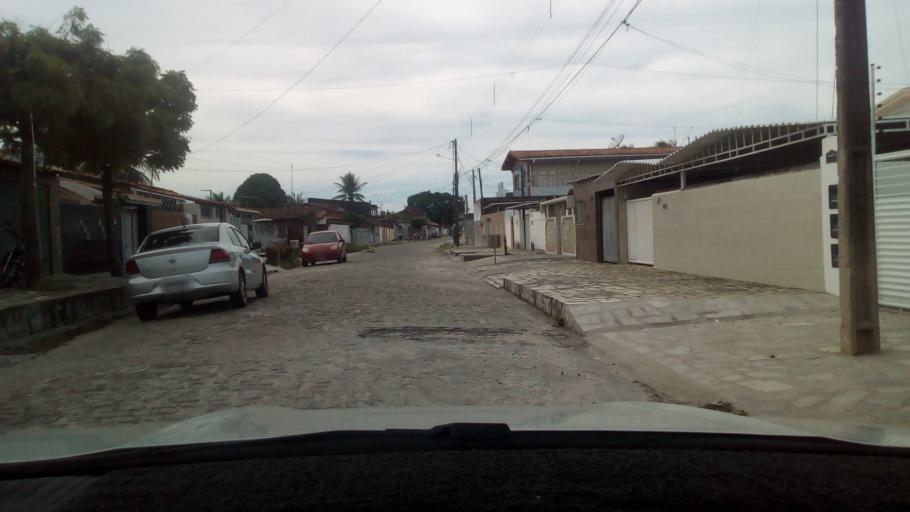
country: BR
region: Paraiba
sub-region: Joao Pessoa
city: Joao Pessoa
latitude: -7.1567
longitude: -34.8687
